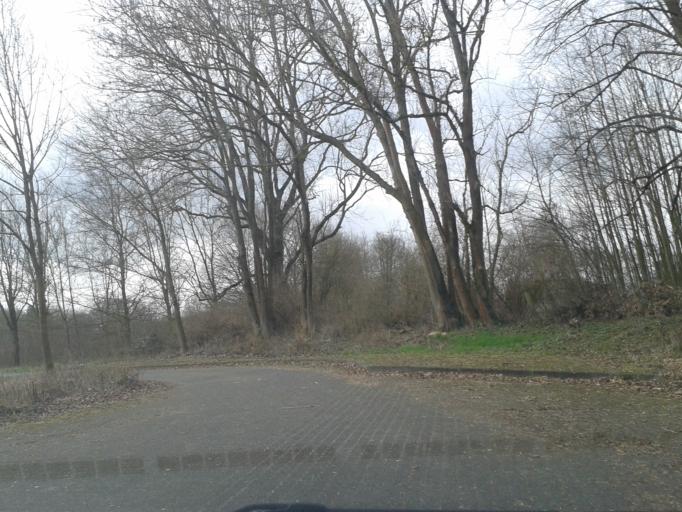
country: DE
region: North Rhine-Westphalia
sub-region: Regierungsbezirk Detmold
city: Schieder-Schwalenberg
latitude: 51.9222
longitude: 9.1547
